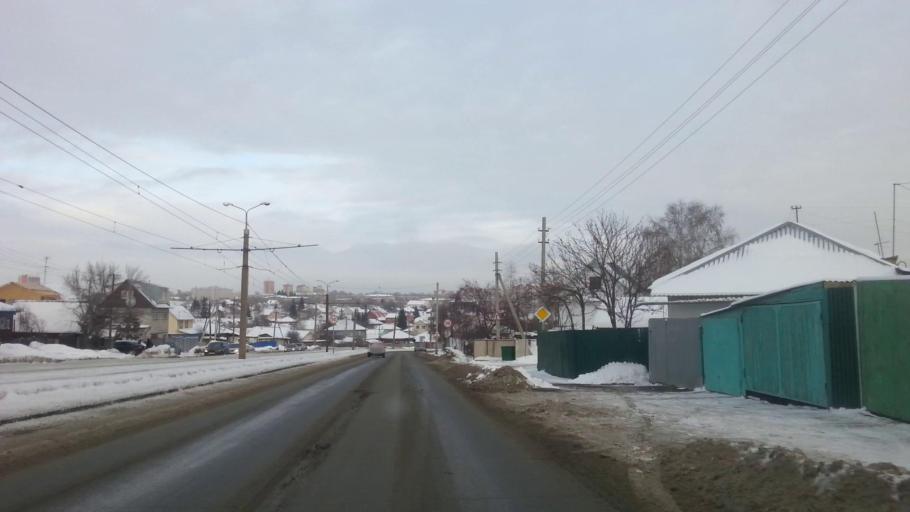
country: RU
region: Altai Krai
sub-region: Gorod Barnaulskiy
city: Barnaul
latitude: 53.3650
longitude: 83.7305
